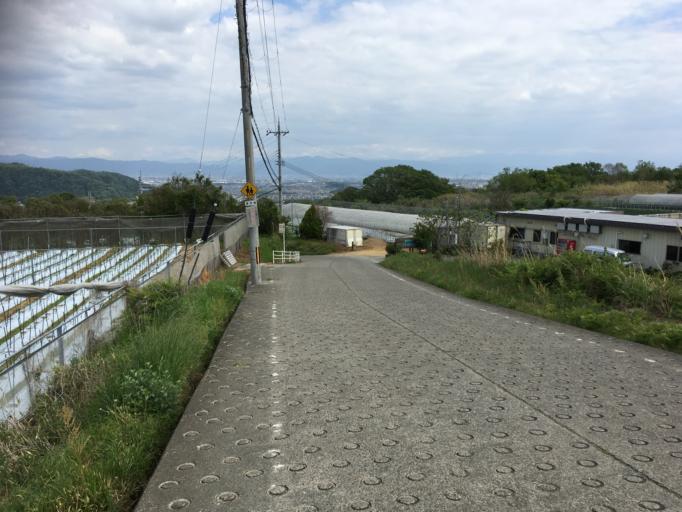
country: JP
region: Nara
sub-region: Ikoma-shi
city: Ikoma
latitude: 34.6265
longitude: 135.6845
